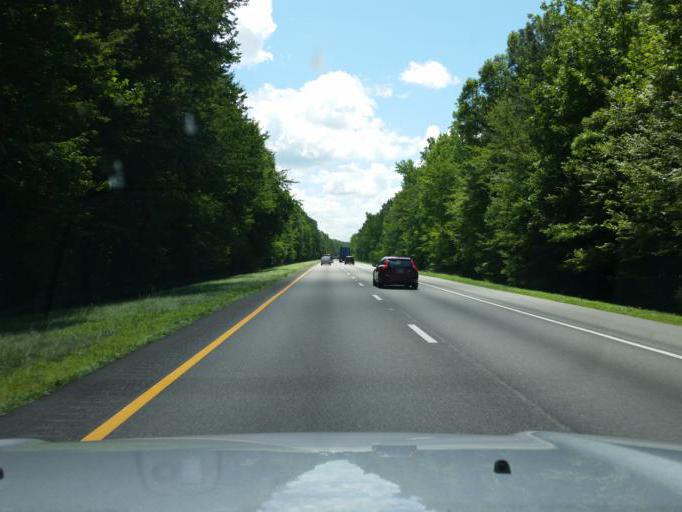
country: US
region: Virginia
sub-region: King William County
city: West Point
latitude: 37.4408
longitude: -76.8550
